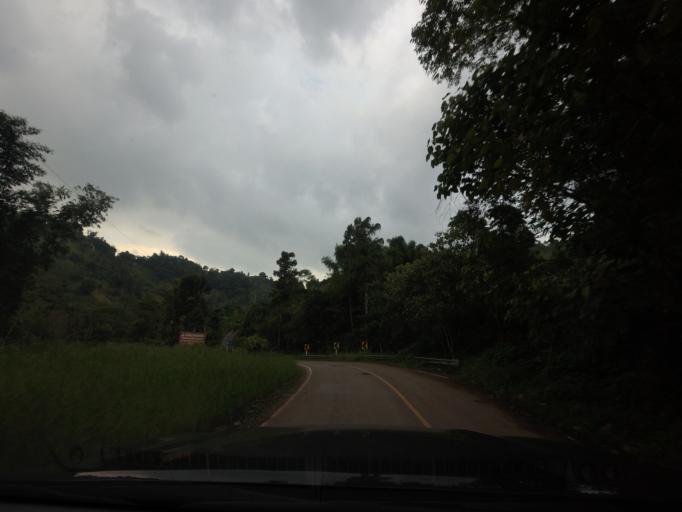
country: TH
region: Nan
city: Bo Kluea
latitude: 19.3513
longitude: 101.1754
